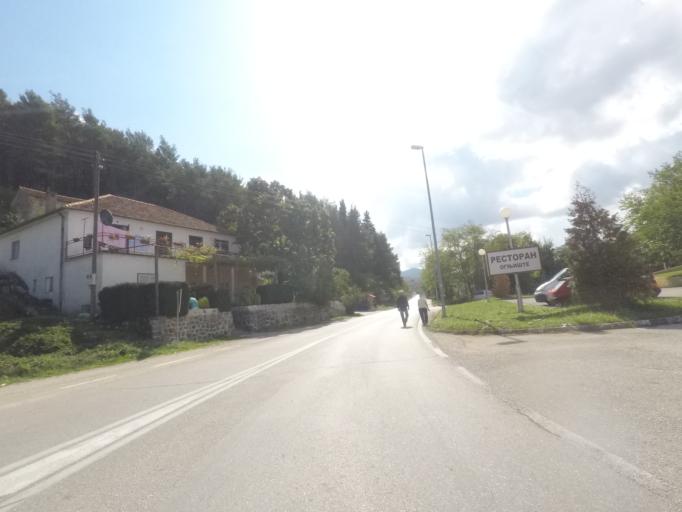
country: BA
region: Republika Srpska
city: Trebinje
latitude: 42.6885
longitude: 18.3364
